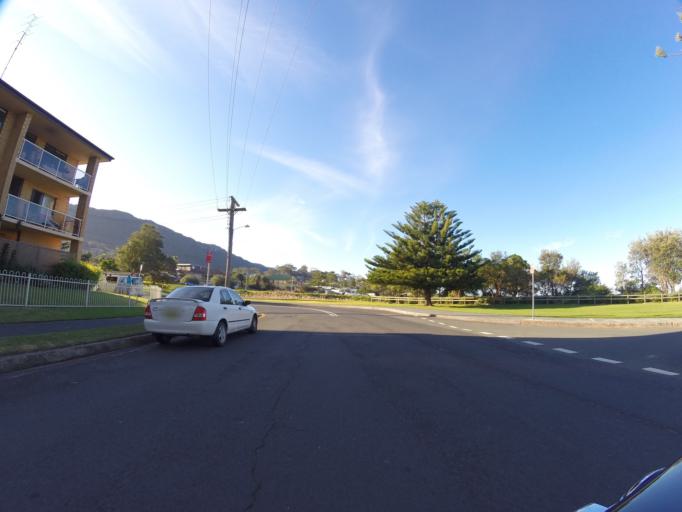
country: AU
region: New South Wales
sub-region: Wollongong
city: Bulli
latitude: -34.3149
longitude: 150.9279
